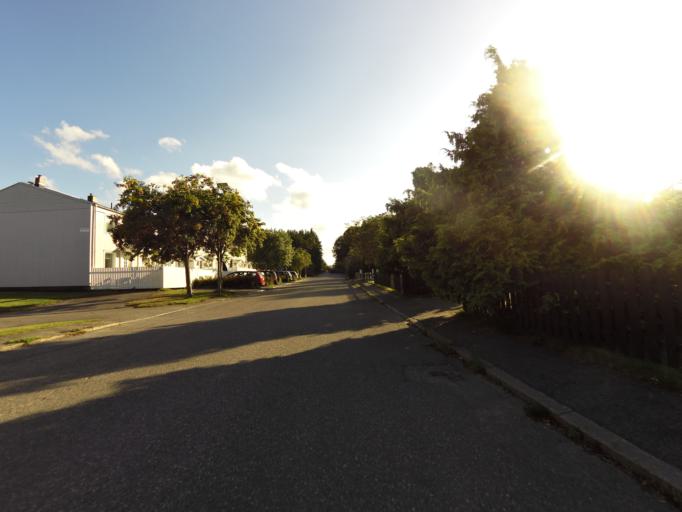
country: SE
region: Gaevleborg
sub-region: Gavle Kommun
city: Gavle
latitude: 60.6513
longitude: 17.1273
